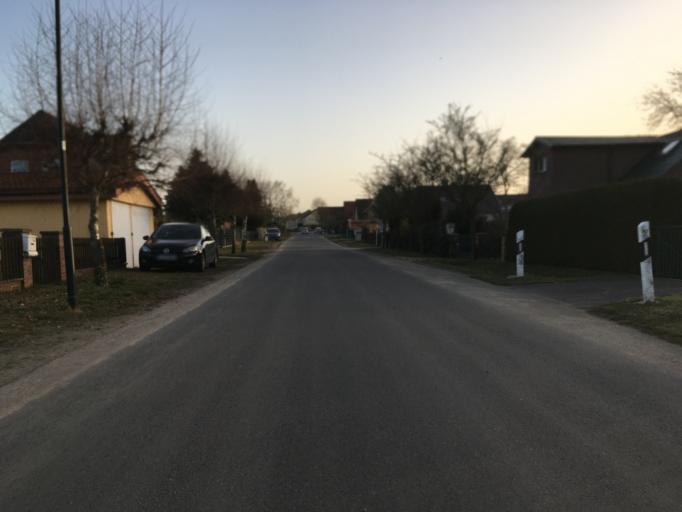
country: DE
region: Berlin
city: Buch
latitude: 52.6339
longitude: 13.5273
